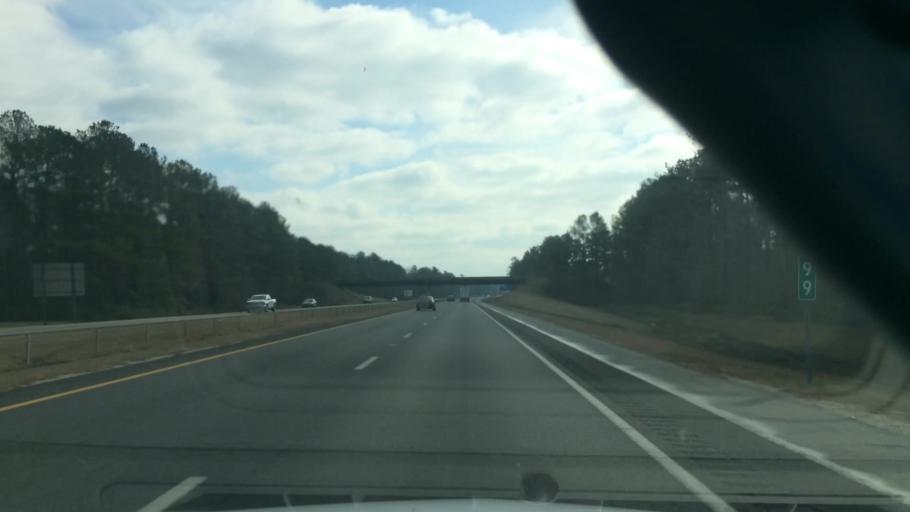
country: US
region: North Carolina
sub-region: Pender County
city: Burgaw
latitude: 34.5678
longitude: -77.8986
